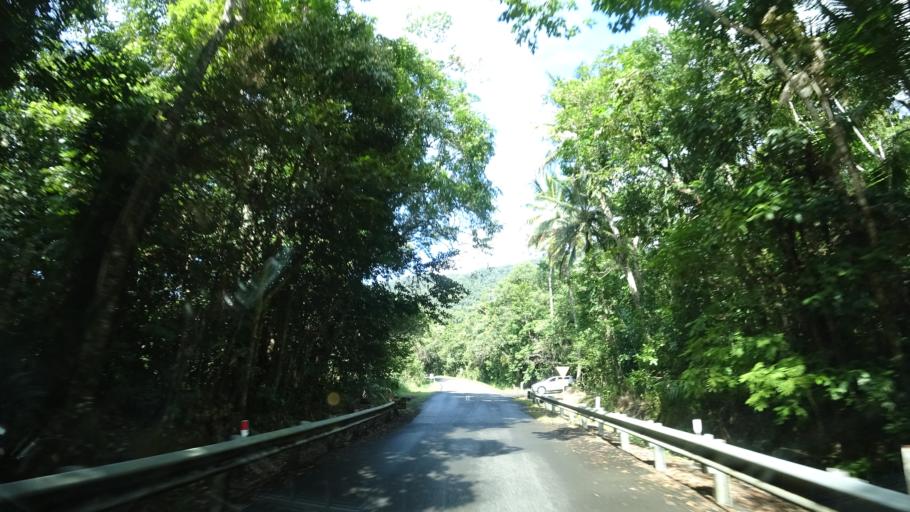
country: AU
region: Queensland
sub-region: Cairns
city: Port Douglas
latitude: -16.1403
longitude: 145.4306
